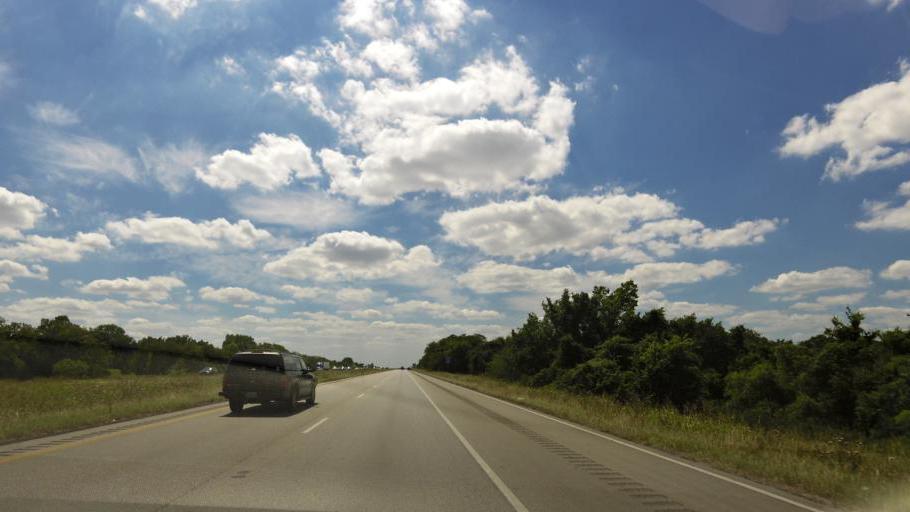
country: US
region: Texas
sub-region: Fayette County
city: Flatonia
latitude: 29.6967
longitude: -97.1150
